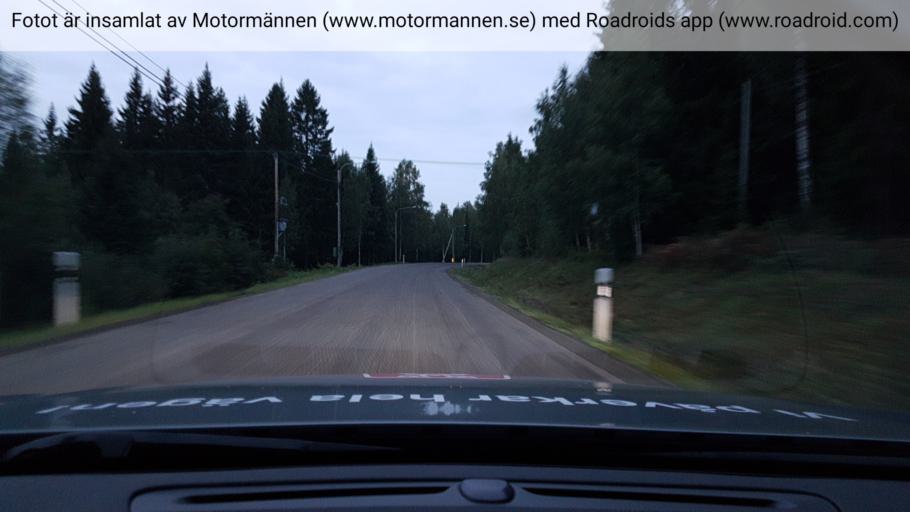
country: SE
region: OErebro
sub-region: Nora Kommun
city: As
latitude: 59.4614
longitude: 14.8499
